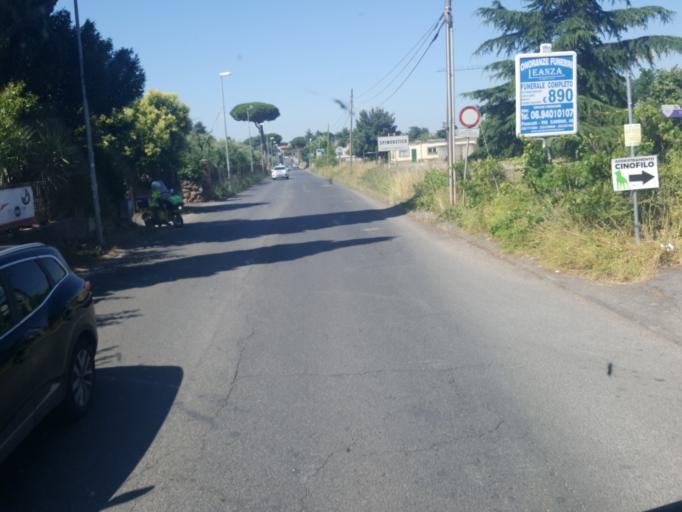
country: IT
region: Latium
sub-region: Citta metropolitana di Roma Capitale
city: Frascati
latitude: 41.8285
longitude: 12.6504
